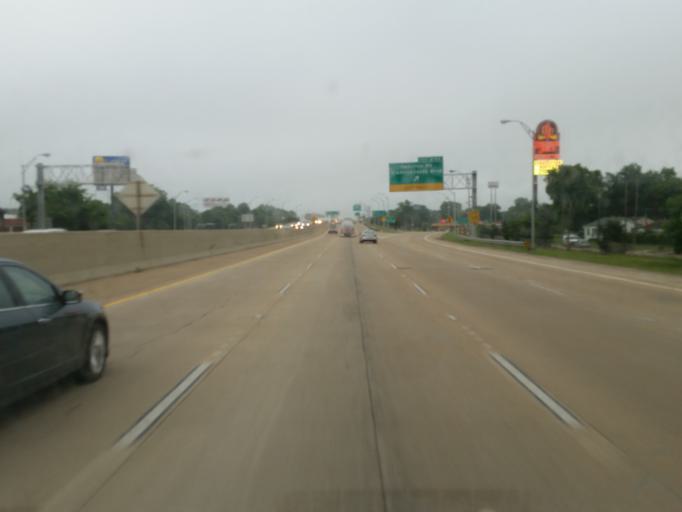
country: US
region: Louisiana
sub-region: Bossier Parish
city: Bossier City
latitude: 32.5139
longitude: -93.7299
